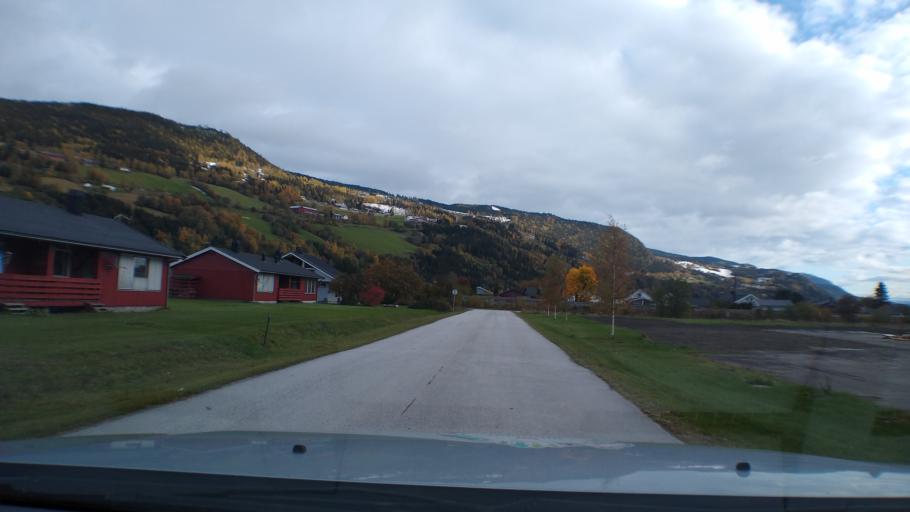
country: NO
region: Oppland
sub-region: Ringebu
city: Ringebu
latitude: 61.5246
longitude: 10.1467
